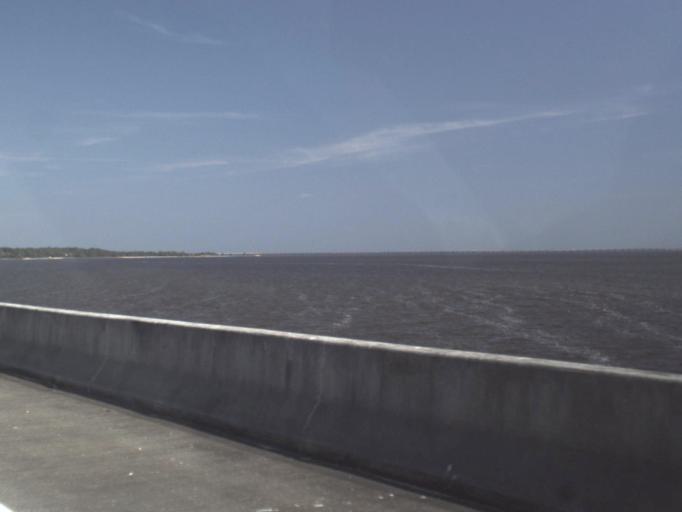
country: US
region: Florida
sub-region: Franklin County
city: Eastpoint
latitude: 29.7329
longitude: -84.9187
